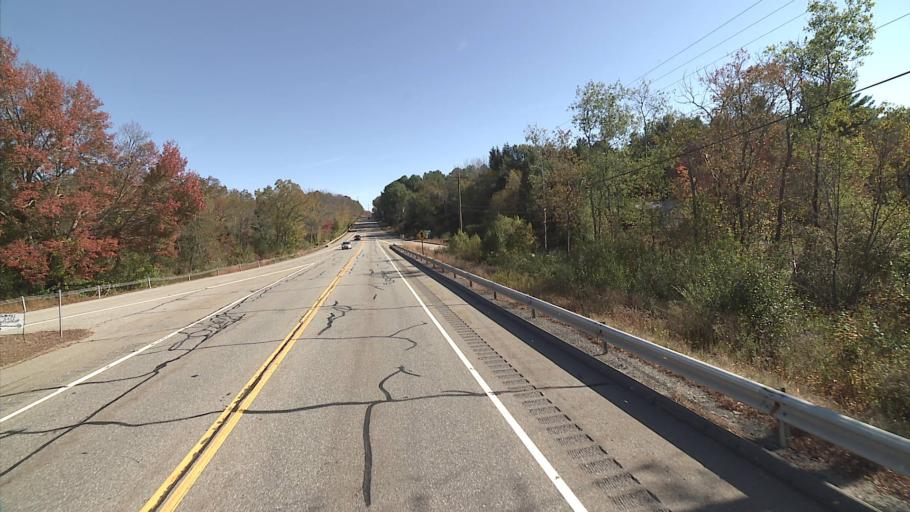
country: US
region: Connecticut
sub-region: Windham County
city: Danielson
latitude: 41.7894
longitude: -71.8442
